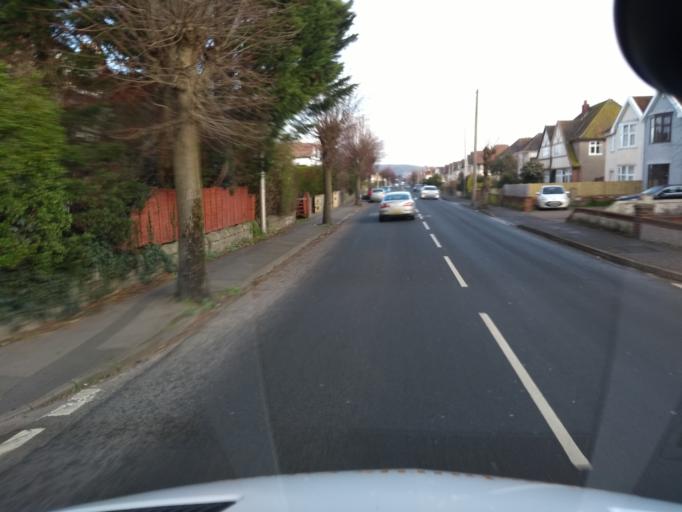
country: GB
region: England
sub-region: North Somerset
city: Weston-super-Mare
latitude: 51.3303
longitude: -2.9741
